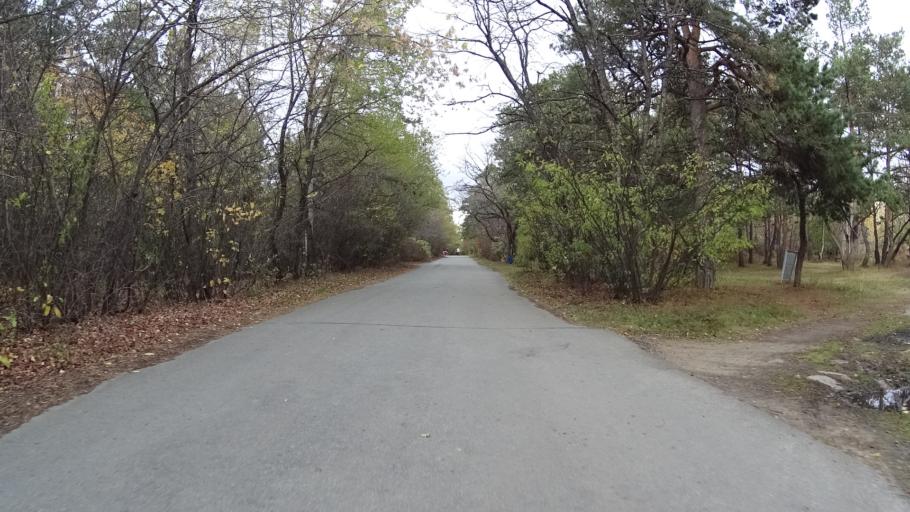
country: RU
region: Chelyabinsk
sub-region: Gorod Chelyabinsk
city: Chelyabinsk
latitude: 55.1484
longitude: 61.3551
